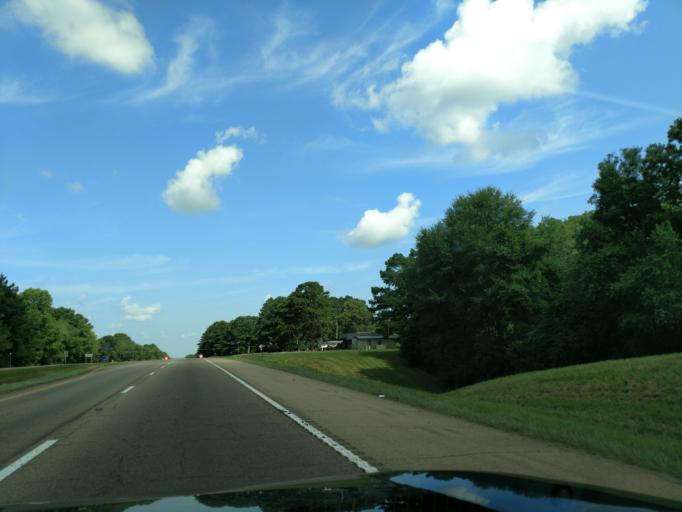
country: US
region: Mississippi
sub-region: Simpson County
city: Magee
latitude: 31.9044
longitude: -89.7809
